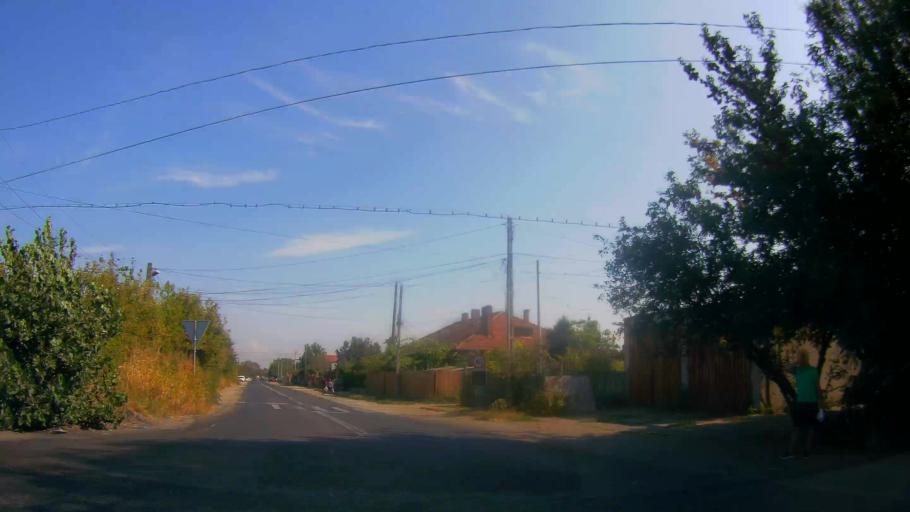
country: RO
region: Giurgiu
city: Giurgiu
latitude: 43.9079
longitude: 25.9814
